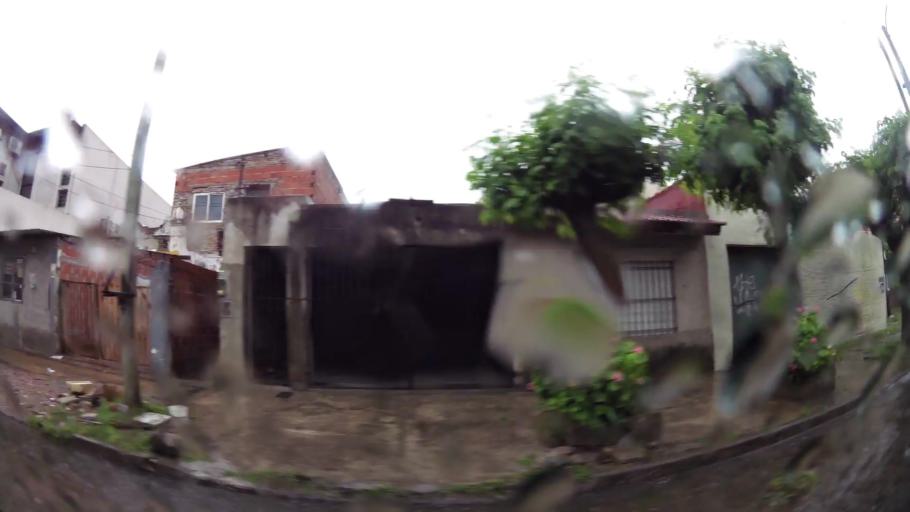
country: AR
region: Buenos Aires
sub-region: Partido de Lanus
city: Lanus
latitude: -34.7104
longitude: -58.4174
